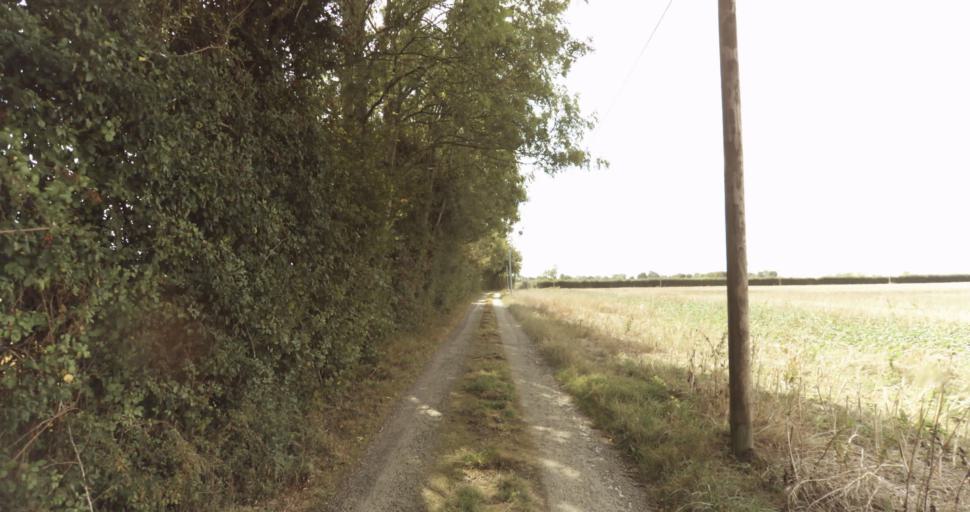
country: FR
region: Lower Normandy
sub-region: Departement du Calvados
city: Orbec
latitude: 48.9501
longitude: 0.4041
